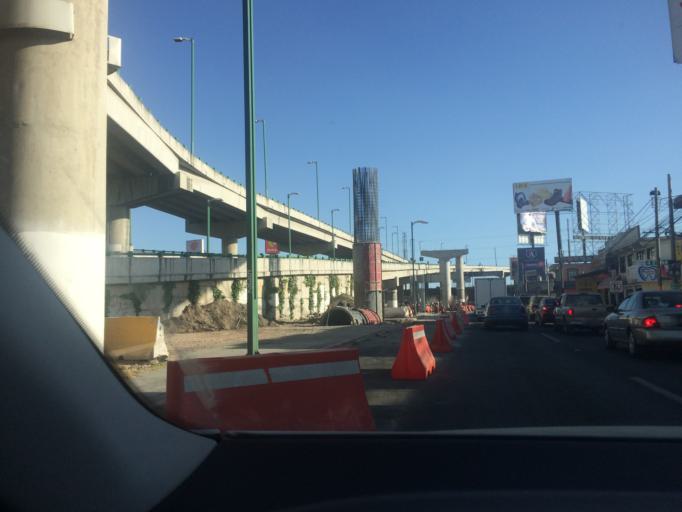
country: MX
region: Mexico
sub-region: San Mateo Atenco
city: Santa Maria la Asuncion
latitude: 19.2890
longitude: -99.5567
